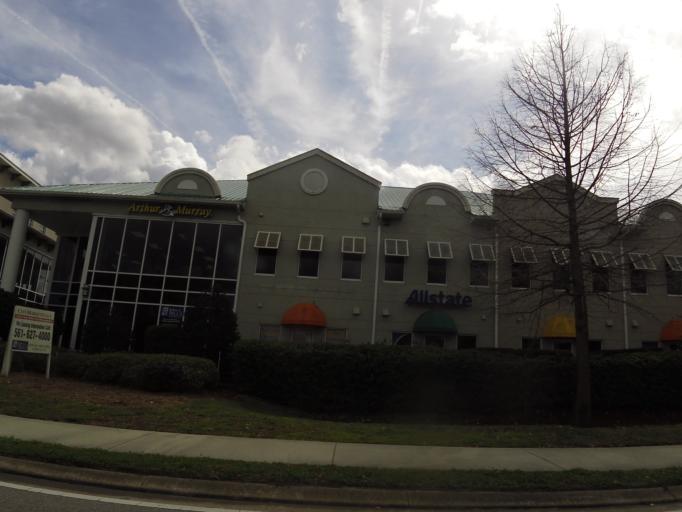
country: US
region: Florida
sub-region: Flagler County
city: Palm Coast
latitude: 29.5493
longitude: -81.2287
